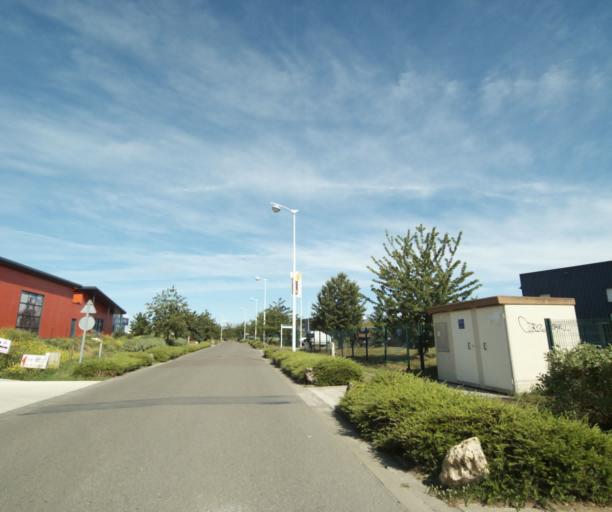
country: FR
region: Centre
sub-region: Departement d'Eure-et-Loir
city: Luce
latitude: 48.4225
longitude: 1.4412
